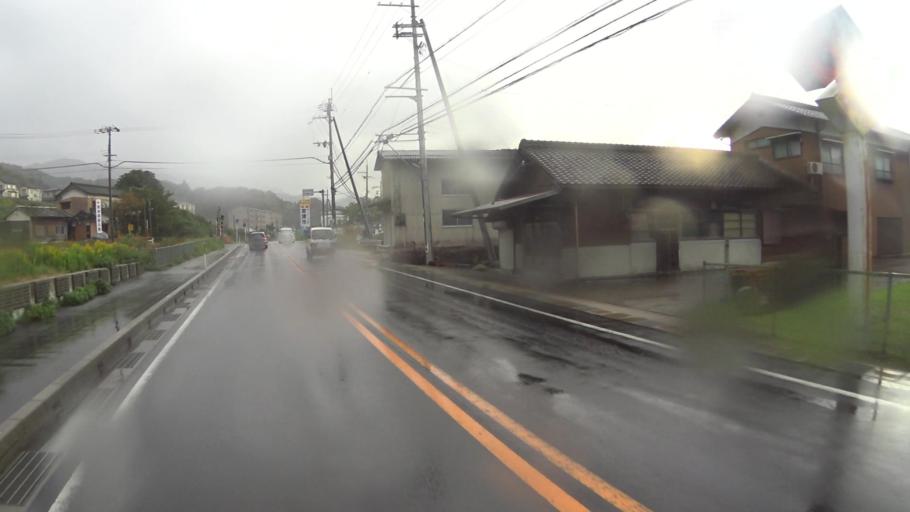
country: JP
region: Kyoto
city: Miyazu
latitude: 35.5455
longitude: 135.2107
